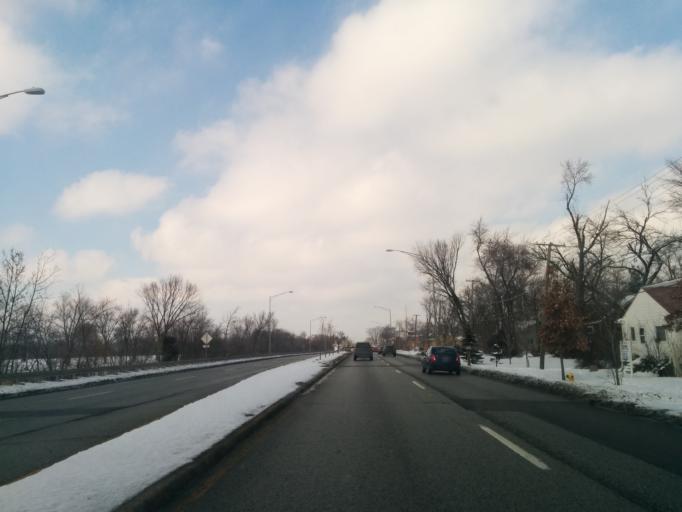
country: US
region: Illinois
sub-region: Cook County
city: Tinley Park
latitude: 41.5664
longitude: -87.7929
